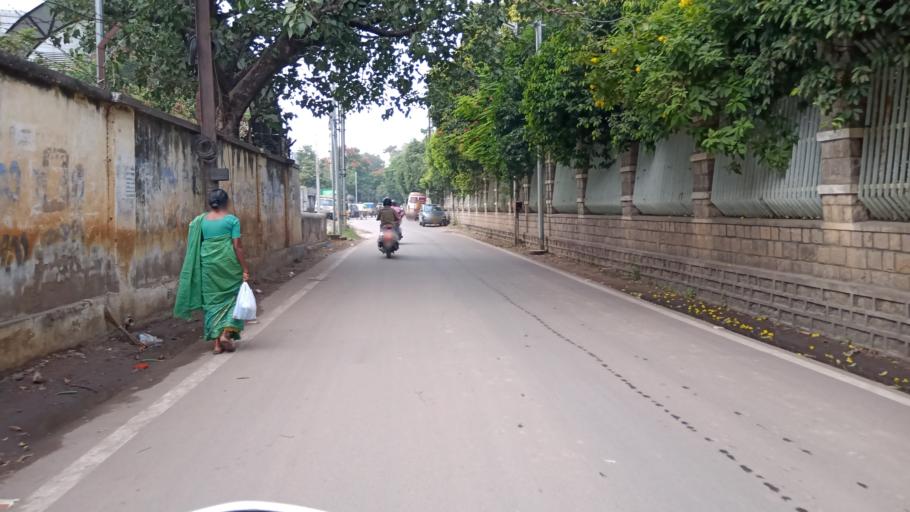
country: IN
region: Telangana
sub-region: Rangareddi
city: Kukatpalli
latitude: 17.4477
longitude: 78.4415
